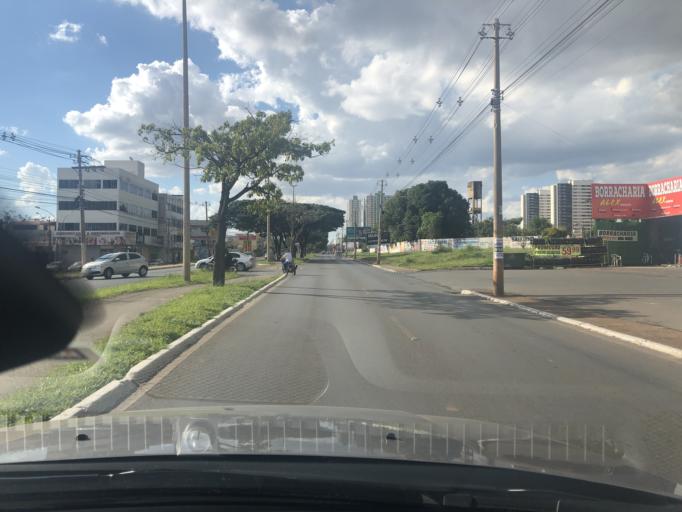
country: BR
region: Federal District
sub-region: Brasilia
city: Brasilia
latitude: -16.0074
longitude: -48.0597
